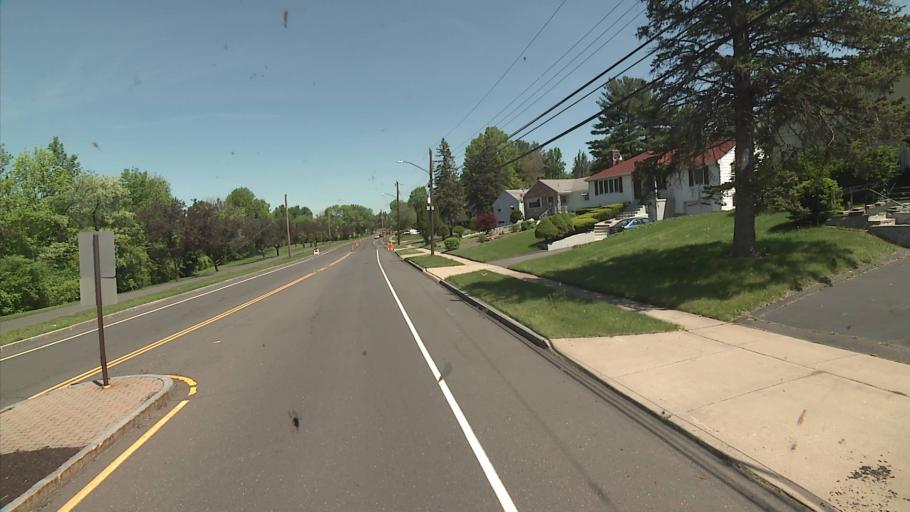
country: US
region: Connecticut
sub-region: Hartford County
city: West Hartford
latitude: 41.7422
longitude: -72.7336
